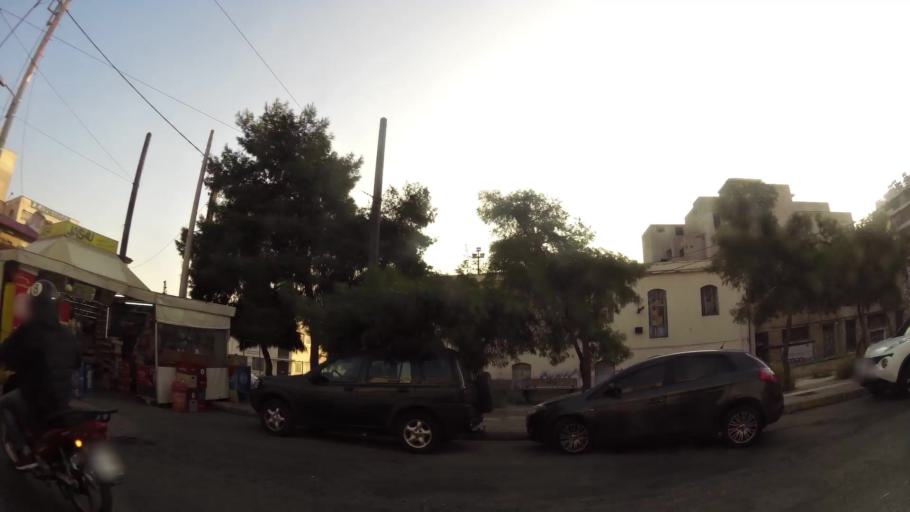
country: GR
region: Attica
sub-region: Nomos Attikis
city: Piraeus
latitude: 37.9512
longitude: 23.6351
